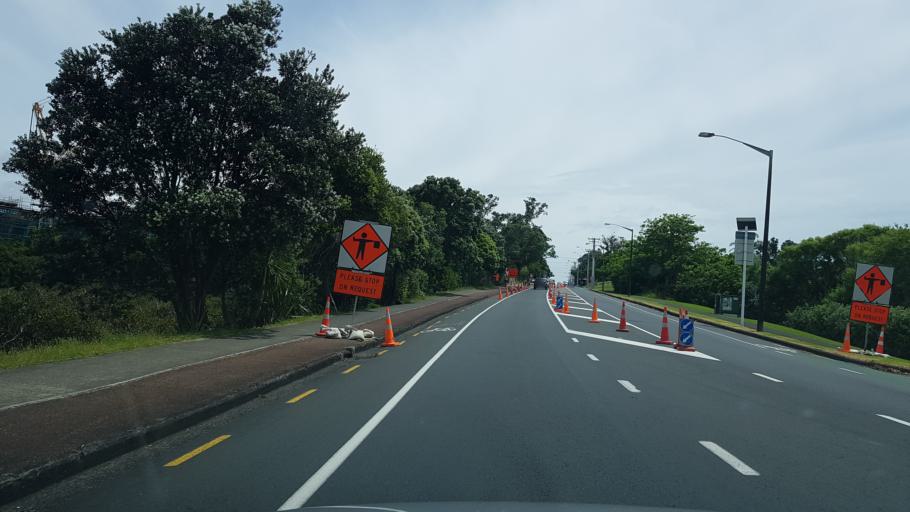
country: NZ
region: Auckland
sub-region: Auckland
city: North Shore
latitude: -36.8179
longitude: 174.7947
